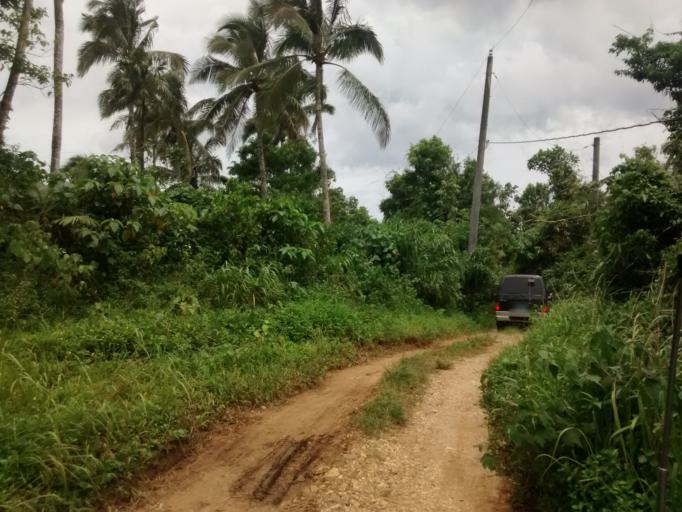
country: PH
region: Calabarzon
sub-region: Province of Quezon
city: Lucban
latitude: 14.1518
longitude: 121.5588
